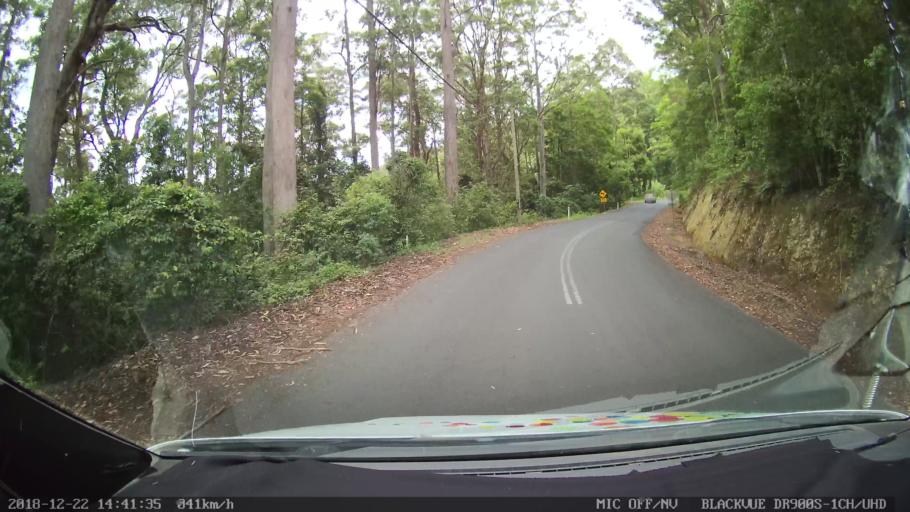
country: AU
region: New South Wales
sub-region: Bellingen
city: Dorrigo
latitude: -30.1554
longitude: 152.5886
